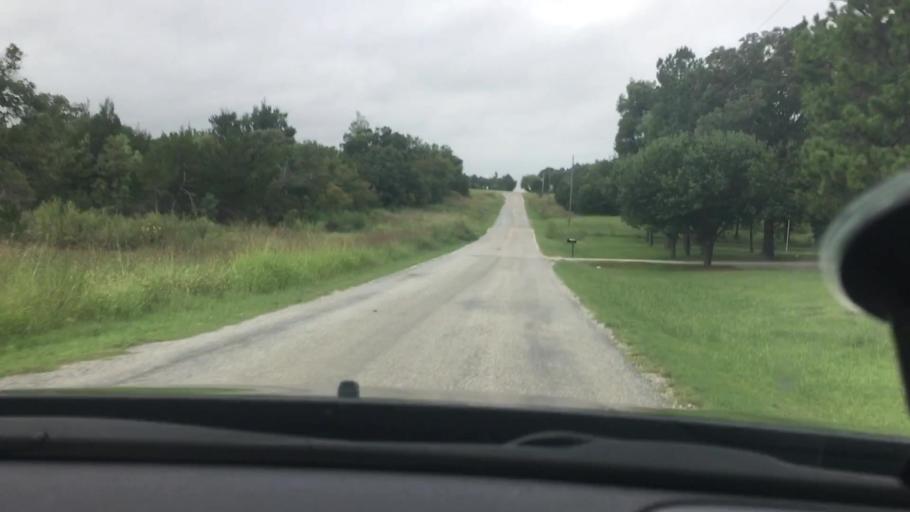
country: US
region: Oklahoma
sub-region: Pontotoc County
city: Byng
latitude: 34.8015
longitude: -96.5475
